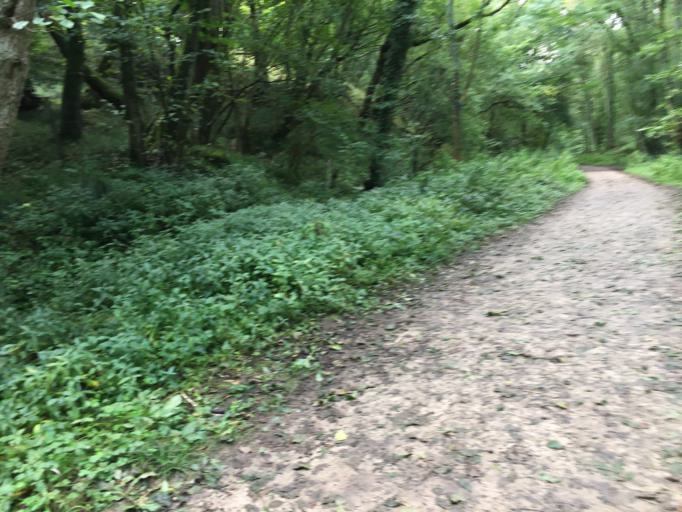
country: GB
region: England
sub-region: North Yorkshire
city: Sleights
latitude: 54.4056
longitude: -0.7296
